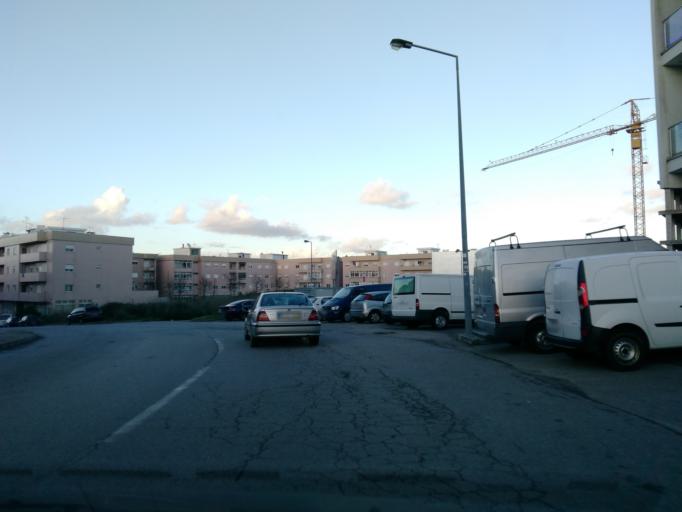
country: PT
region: Braga
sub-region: Braga
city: Braga
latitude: 41.5333
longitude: -8.4531
